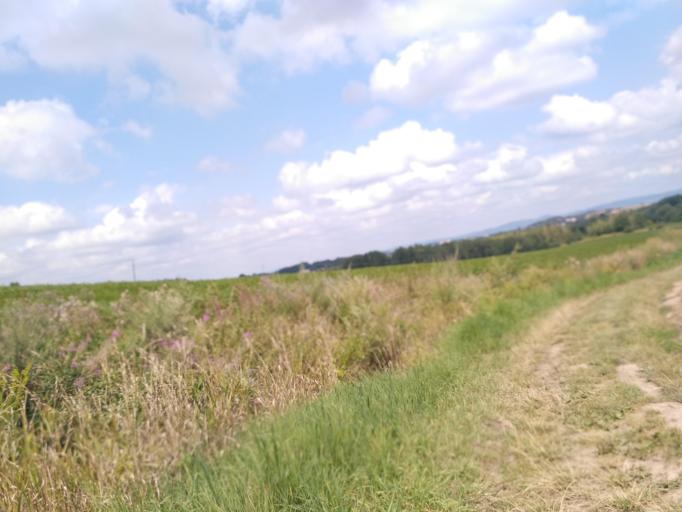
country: PL
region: Subcarpathian Voivodeship
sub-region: Powiat krosnienski
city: Iwonicz-Zdroj
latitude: 49.5896
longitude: 21.8079
